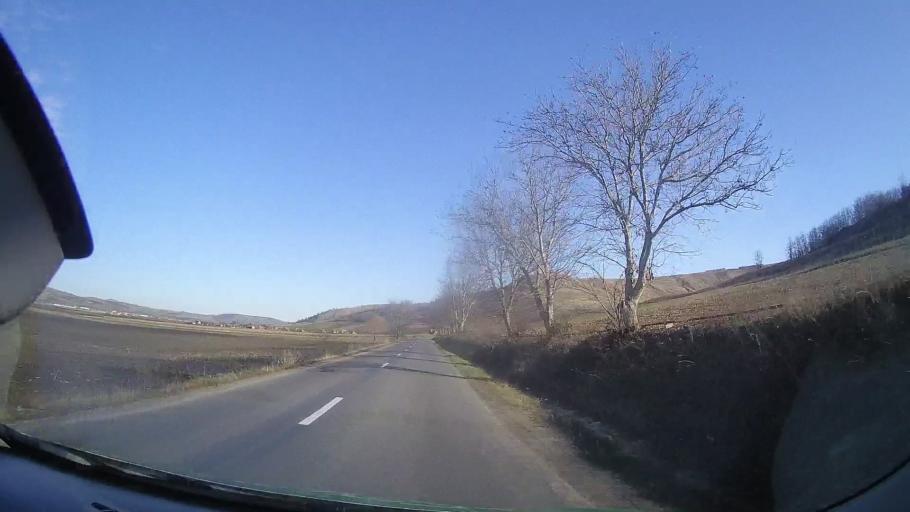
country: RO
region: Mures
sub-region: Comuna Iclanzel
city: Iclanzel
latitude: 46.5508
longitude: 24.3297
